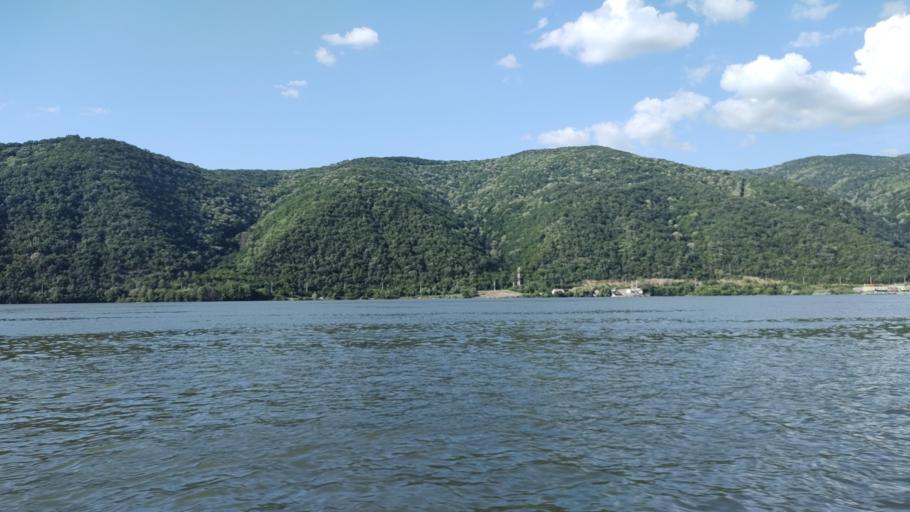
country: RO
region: Caras-Severin
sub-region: Comuna Berzasca
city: Berzasca
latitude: 44.6322
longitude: 21.9868
